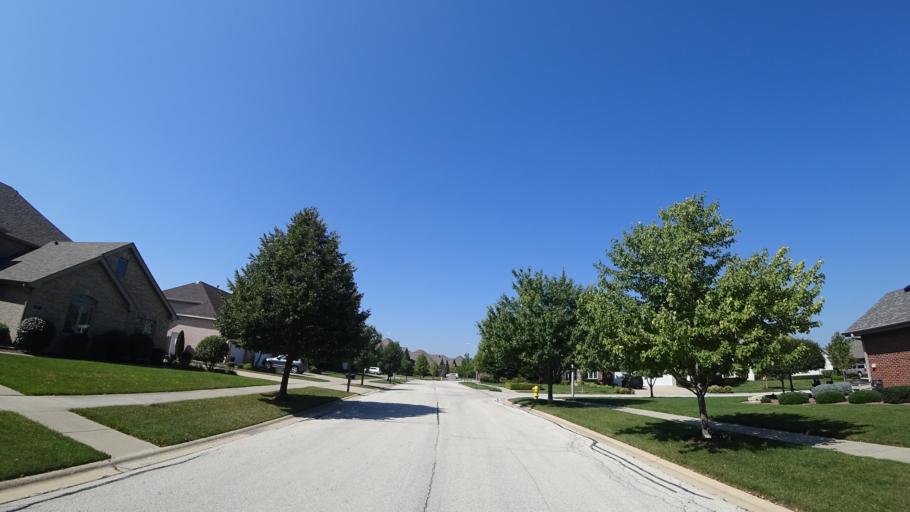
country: US
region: Illinois
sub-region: Cook County
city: Orland Park
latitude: 41.6336
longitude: -87.8284
